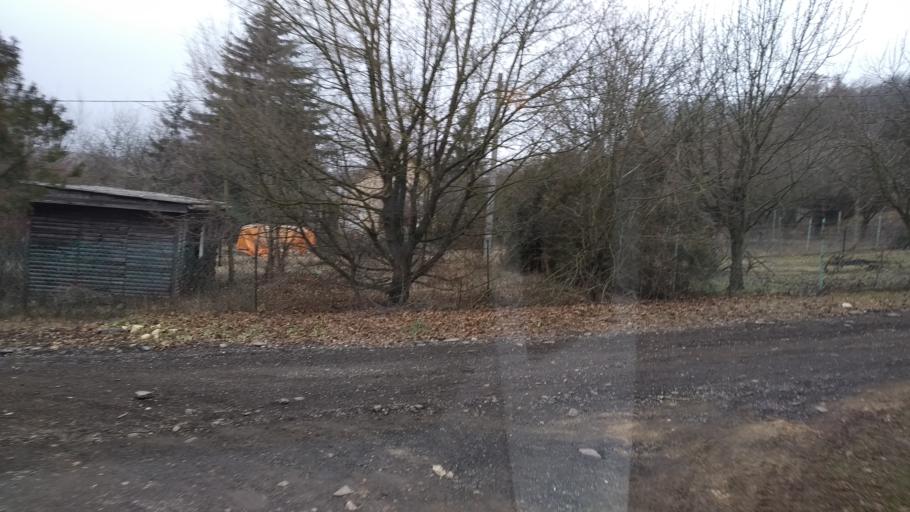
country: HU
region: Pest
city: Solymar
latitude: 47.6074
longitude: 18.9604
